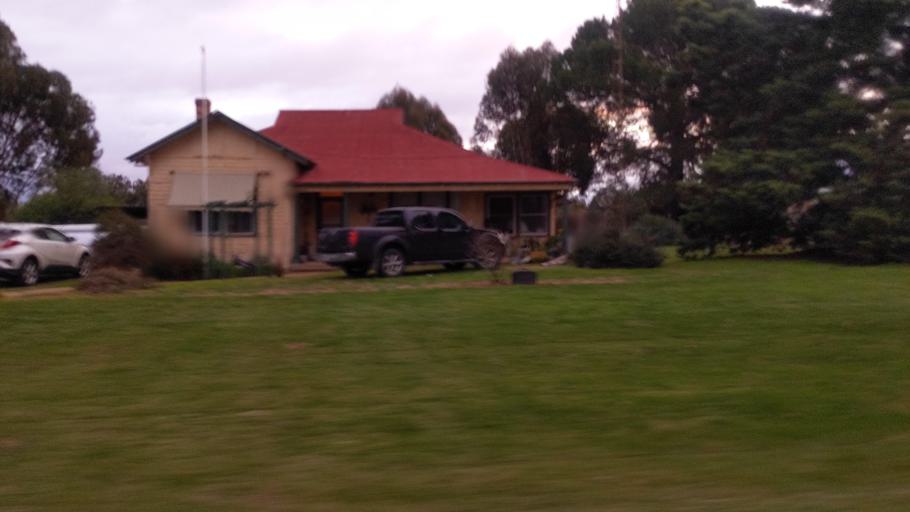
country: AU
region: New South Wales
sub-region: Narrandera
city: Narrandera
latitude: -34.7356
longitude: 146.7834
